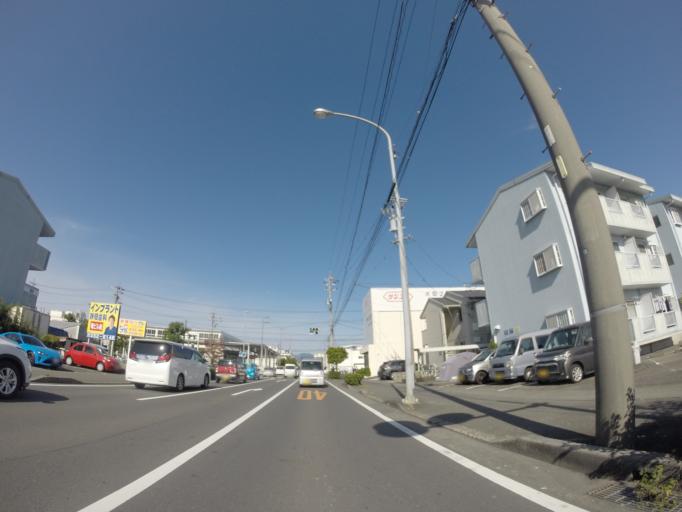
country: JP
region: Shizuoka
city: Shizuoka-shi
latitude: 34.9698
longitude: 138.4203
